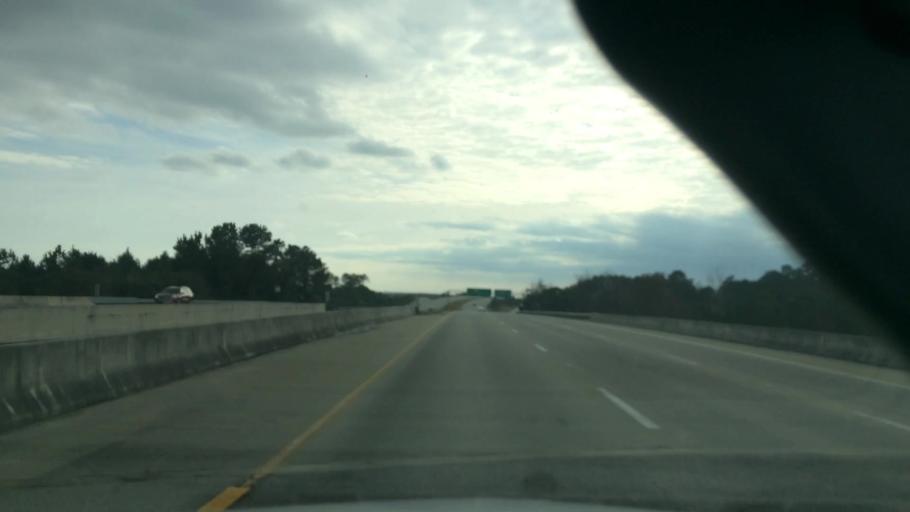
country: US
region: South Carolina
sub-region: Horry County
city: North Myrtle Beach
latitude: 33.8527
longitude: -78.6982
